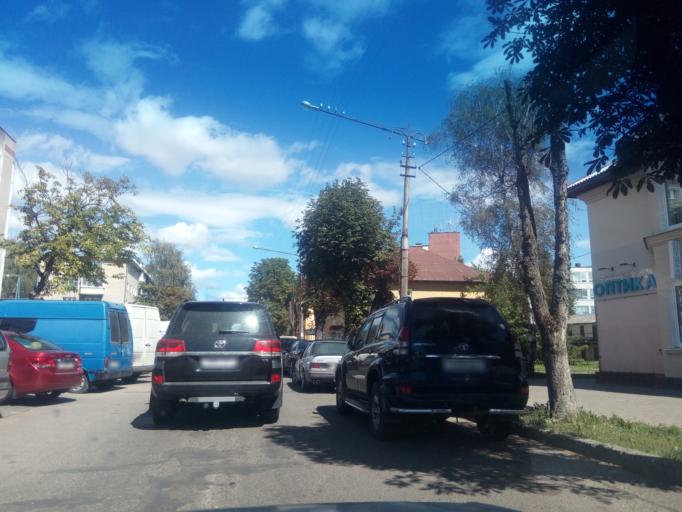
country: BY
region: Vitebsk
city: Polatsk
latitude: 55.4877
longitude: 28.7835
